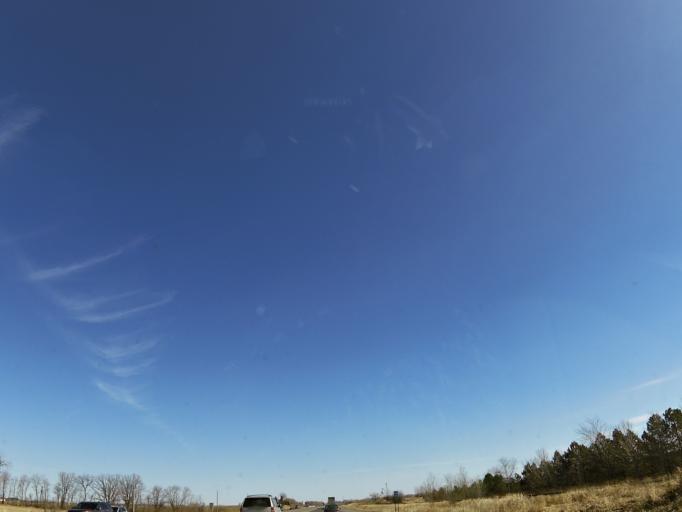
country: US
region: Minnesota
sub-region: Hennepin County
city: Medina
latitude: 45.0510
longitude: -93.5618
